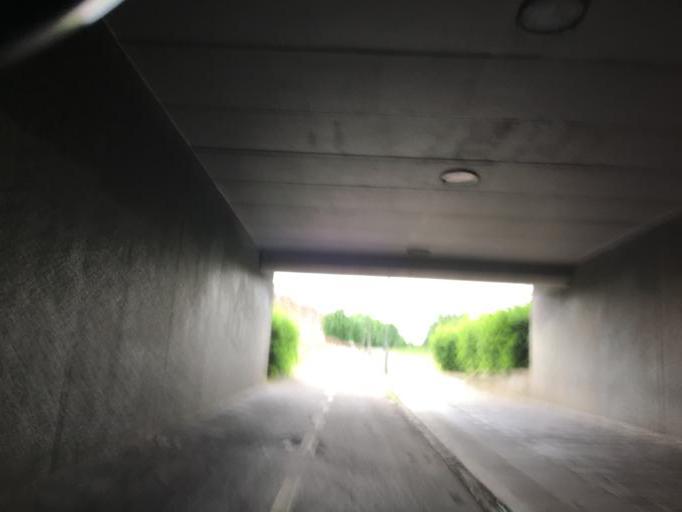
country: SE
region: Skane
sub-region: Malmo
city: Malmoe
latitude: 55.5835
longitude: 13.0339
